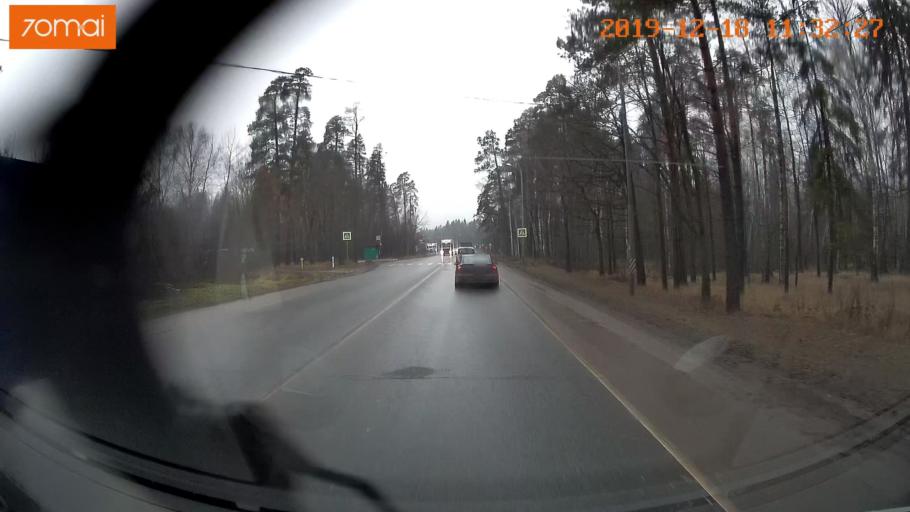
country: RU
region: Moskovskaya
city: Bol'shiye Vyazemy
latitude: 55.6697
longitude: 36.9531
